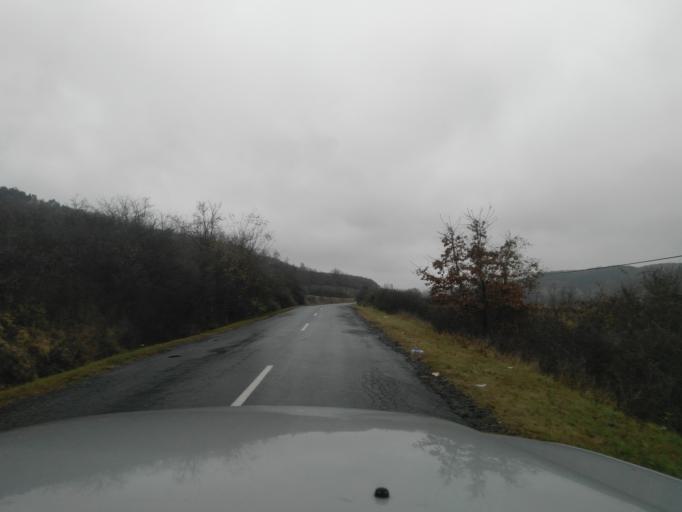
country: HU
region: Nograd
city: Kazar
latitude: 48.0113
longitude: 19.8514
